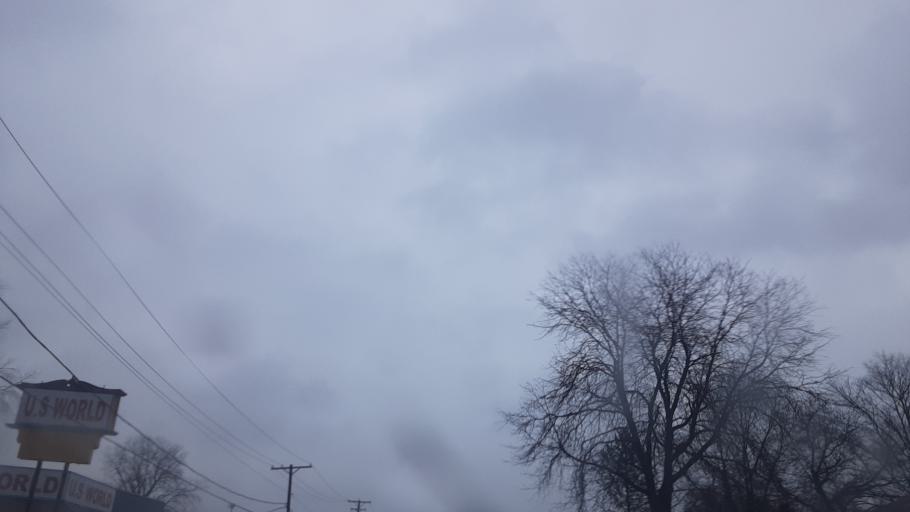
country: US
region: Illinois
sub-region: Winnebago County
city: Rockford
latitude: 42.2884
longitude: -89.1102
